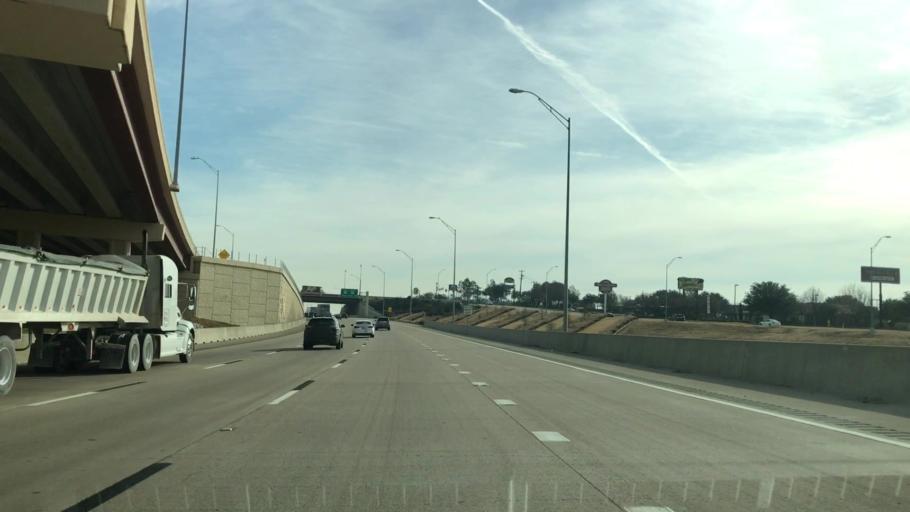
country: US
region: Texas
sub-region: Tarrant County
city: Grapevine
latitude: 32.9229
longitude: -97.0822
